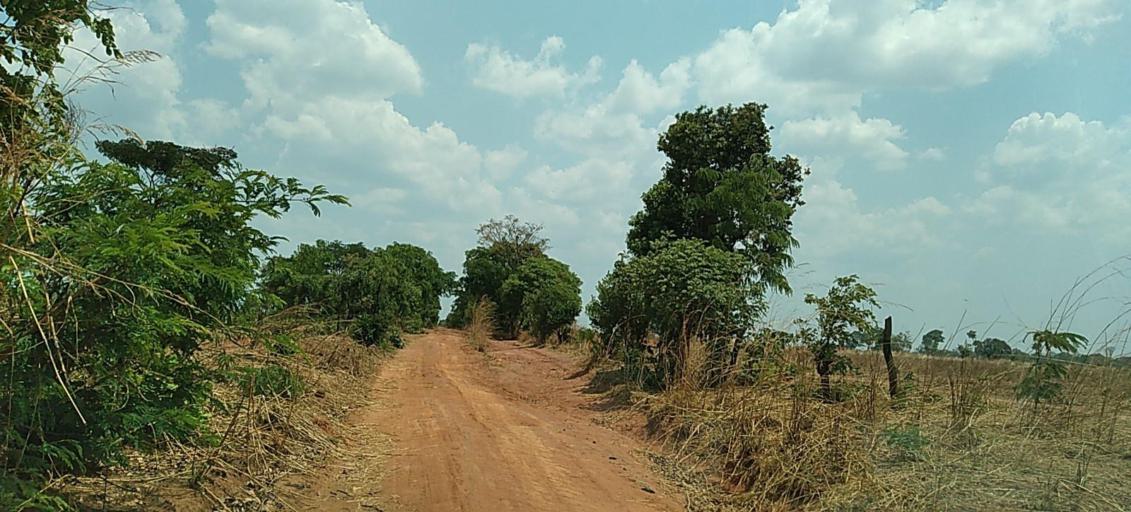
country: ZM
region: Copperbelt
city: Mpongwe
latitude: -13.6570
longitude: 28.0253
